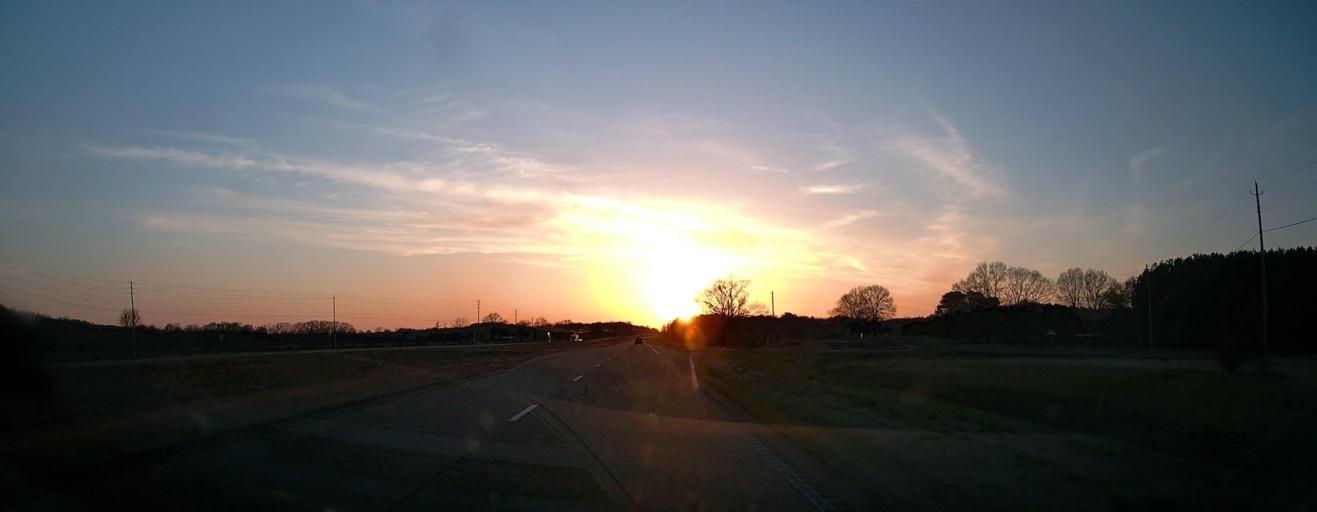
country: US
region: Mississippi
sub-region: Alcorn County
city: Corinth
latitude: 34.9319
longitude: -88.6634
